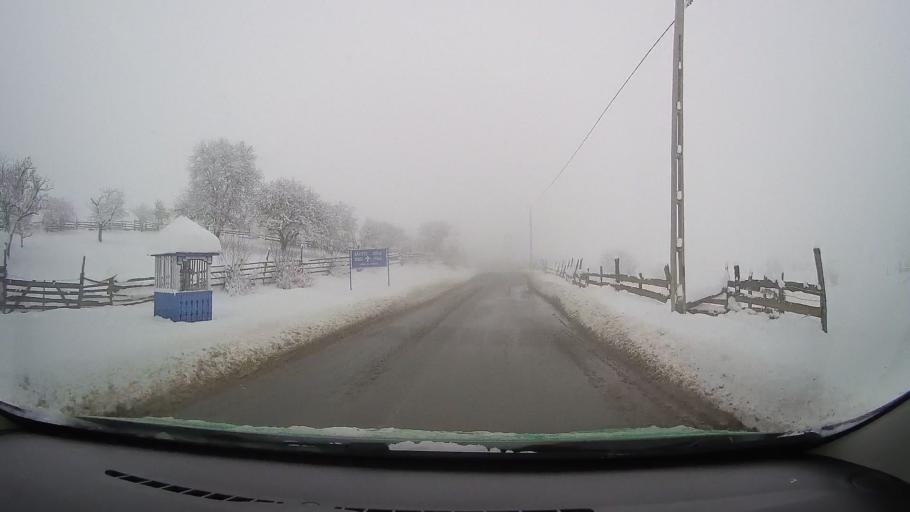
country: RO
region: Sibiu
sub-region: Comuna Jina
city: Jina
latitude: 45.7756
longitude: 23.6663
